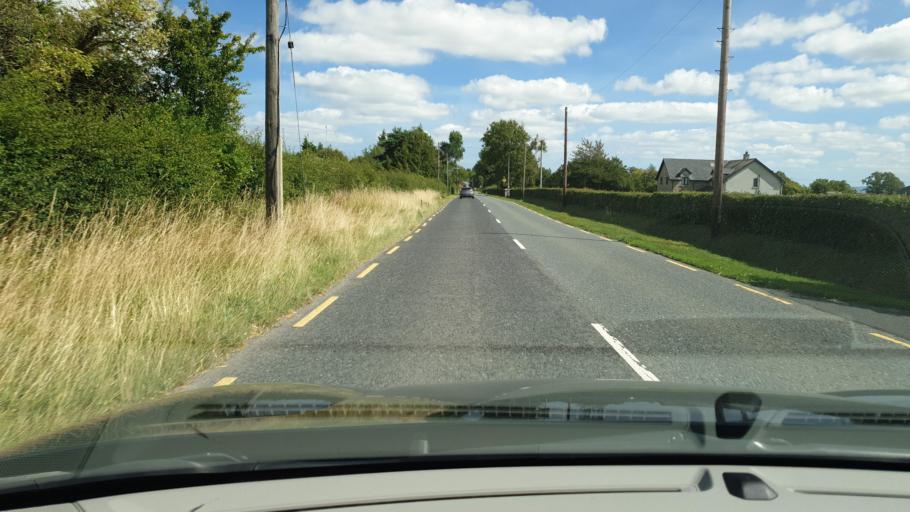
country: IE
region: Leinster
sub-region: An Mhi
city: Dunboyne
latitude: 53.4298
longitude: -6.5051
